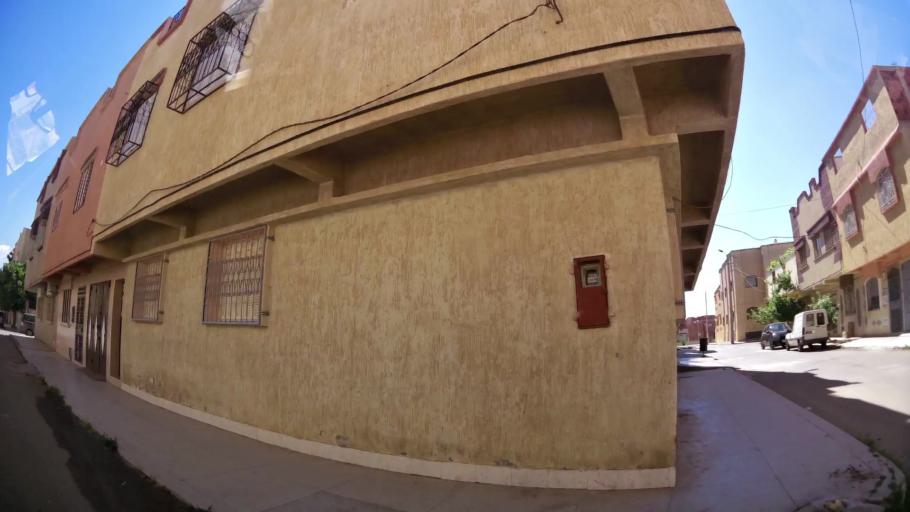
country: MA
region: Oriental
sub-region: Oujda-Angad
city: Oujda
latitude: 34.6623
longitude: -1.9294
